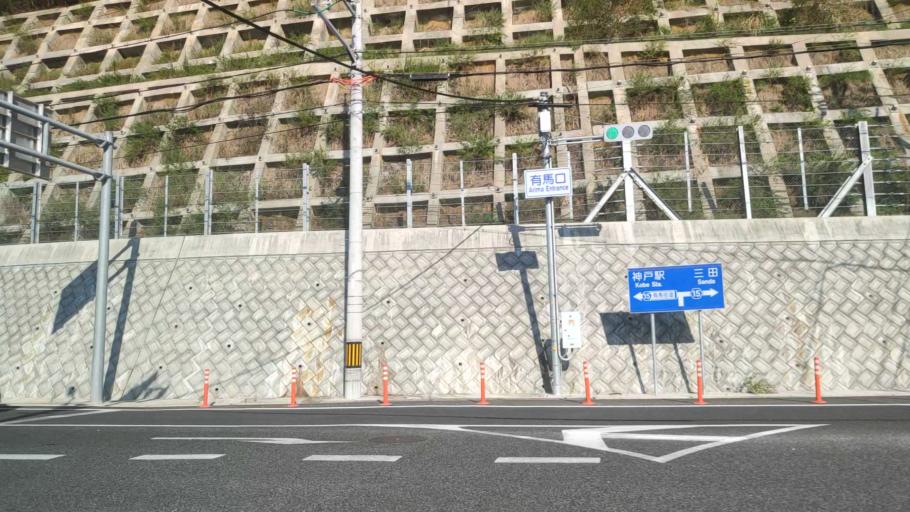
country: JP
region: Hyogo
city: Sandacho
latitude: 34.7969
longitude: 135.2200
